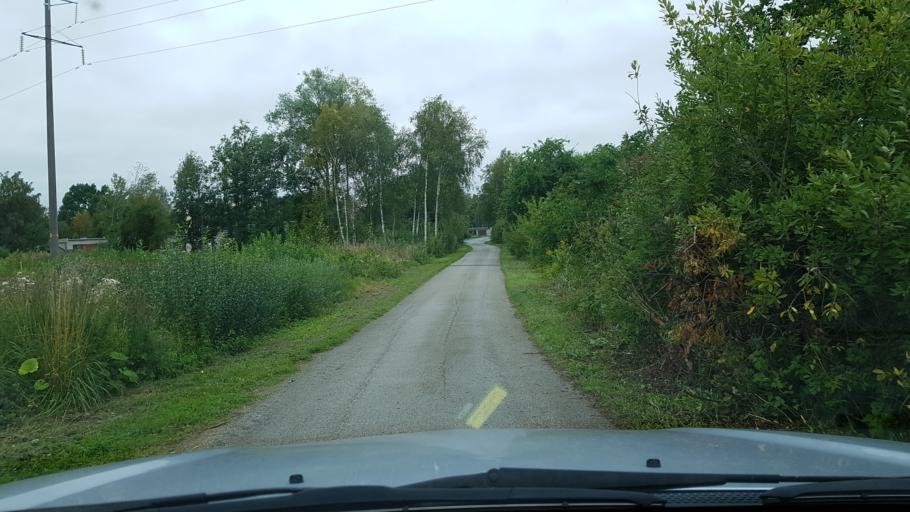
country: EE
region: Harju
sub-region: Rae vald
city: Jueri
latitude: 59.3538
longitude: 24.9186
